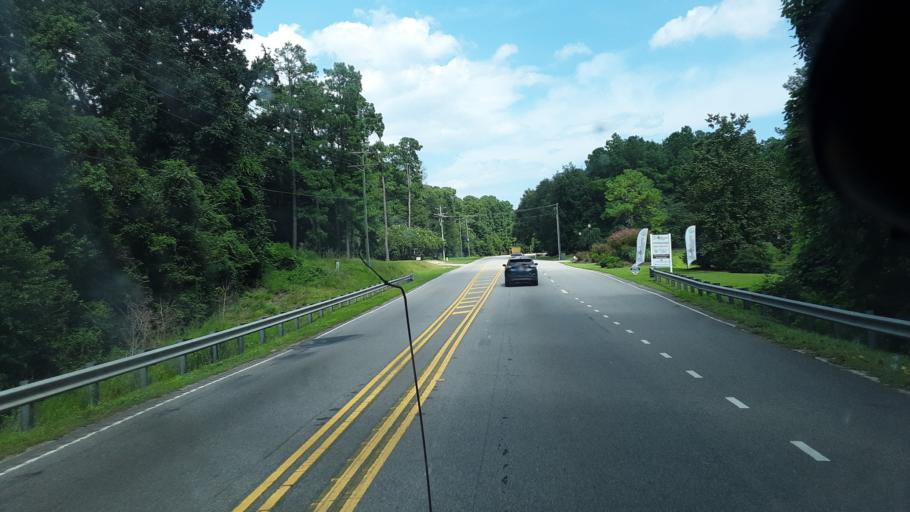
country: US
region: South Carolina
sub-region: Horry County
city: Red Hill
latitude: 33.8218
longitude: -78.9280
